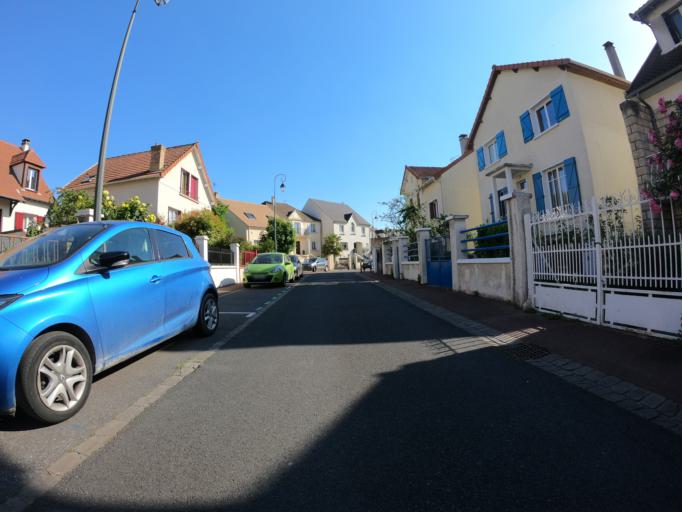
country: FR
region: Ile-de-France
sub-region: Departement des Hauts-de-Seine
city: Antony
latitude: 48.7446
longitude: 2.3019
